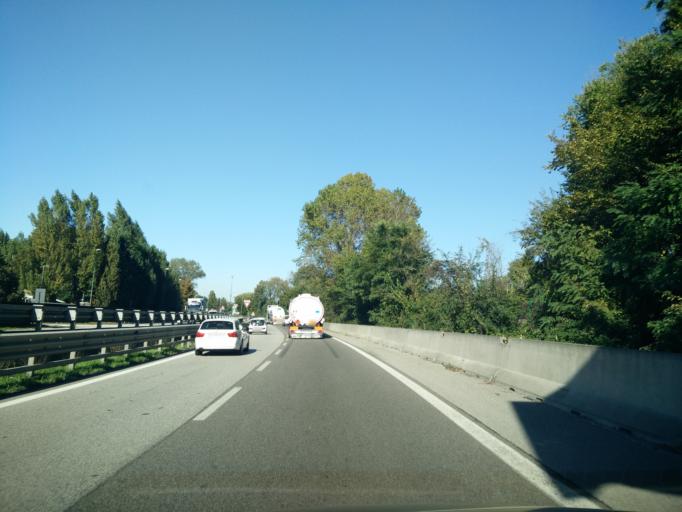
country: IT
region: Veneto
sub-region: Provincia di Venezia
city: Mestre
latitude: 45.4705
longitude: 12.2133
